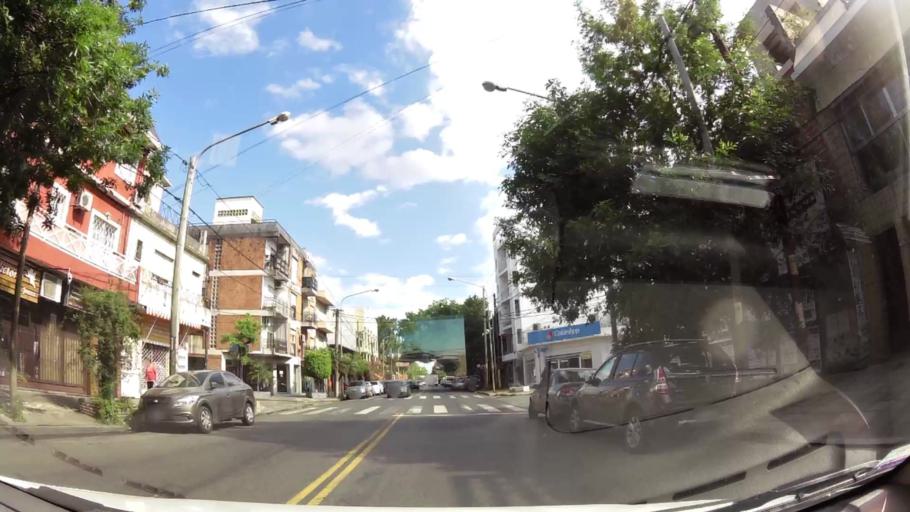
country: AR
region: Buenos Aires
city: San Justo
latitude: -34.6591
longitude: -58.5622
